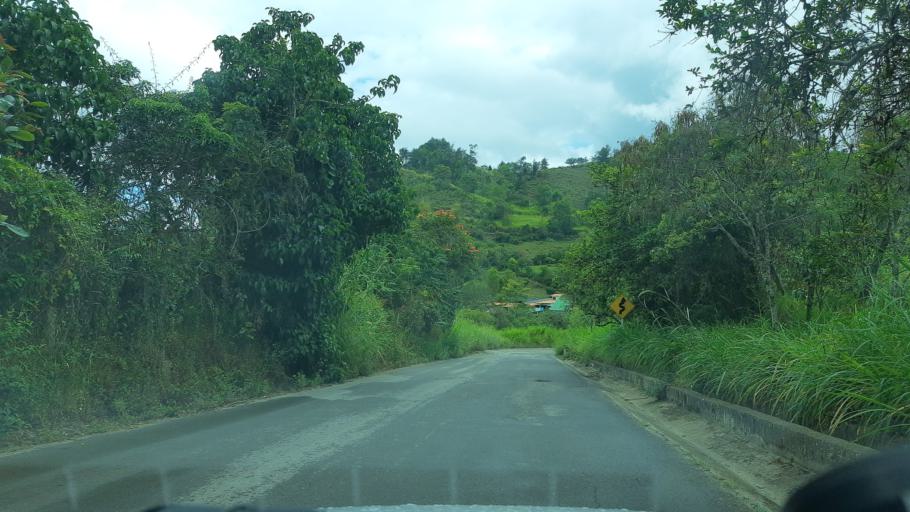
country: CO
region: Cundinamarca
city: Tenza
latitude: 5.0861
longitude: -73.4388
